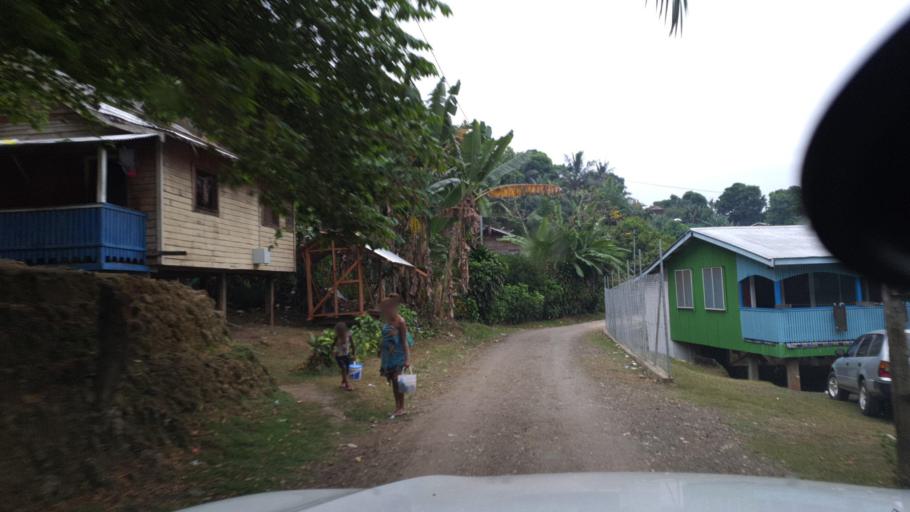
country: SB
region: Guadalcanal
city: Honiara
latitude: -9.4547
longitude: 159.9848
